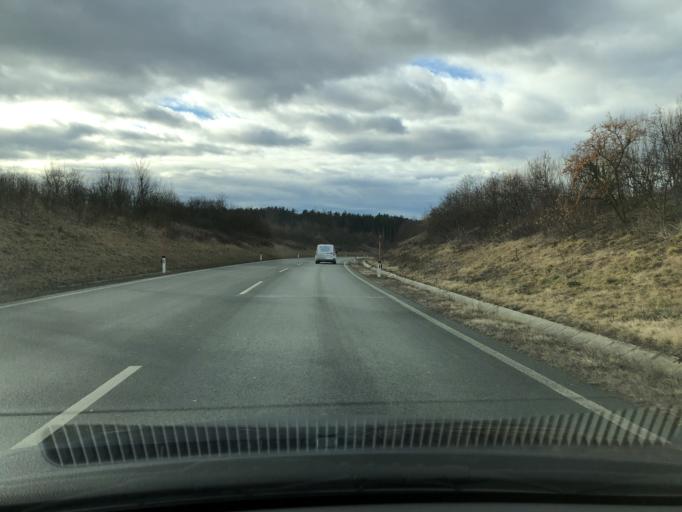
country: AT
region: Burgenland
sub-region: Politischer Bezirk Oberwart
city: Hannersdorf
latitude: 47.2645
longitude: 16.3773
